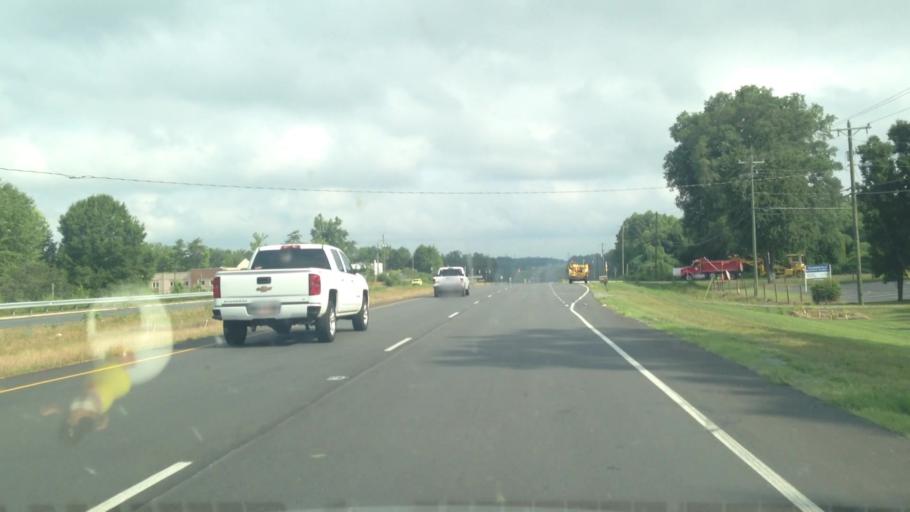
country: US
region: North Carolina
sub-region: Guilford County
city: Summerfield
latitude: 36.2168
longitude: -79.9084
